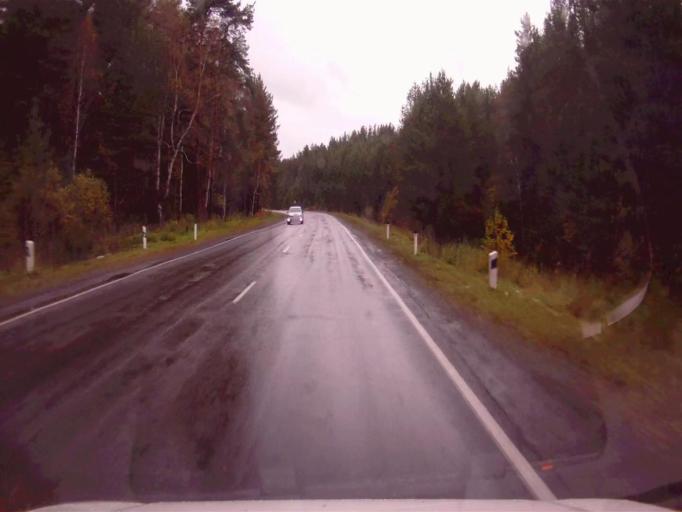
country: RU
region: Chelyabinsk
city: Verkhniy Ufaley
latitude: 56.0231
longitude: 60.2994
